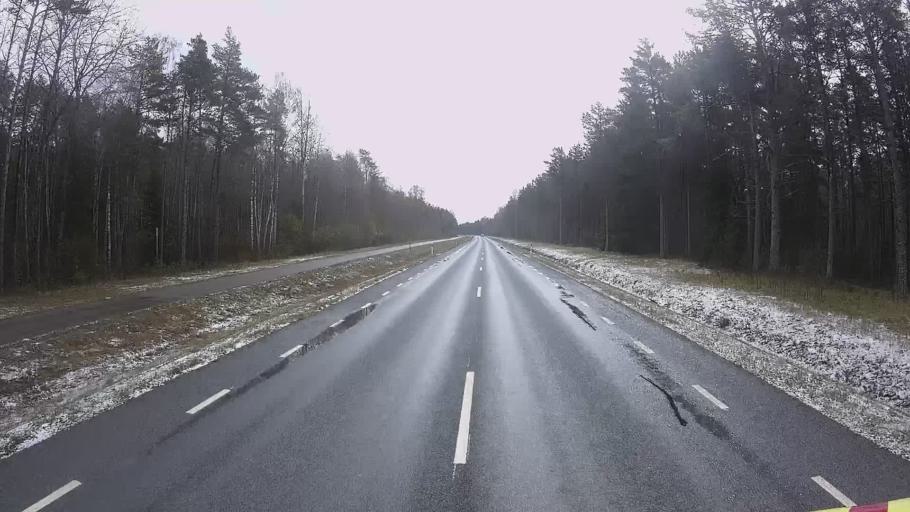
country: EE
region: Hiiumaa
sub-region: Kaerdla linn
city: Kardla
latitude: 59.0010
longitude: 22.6983
